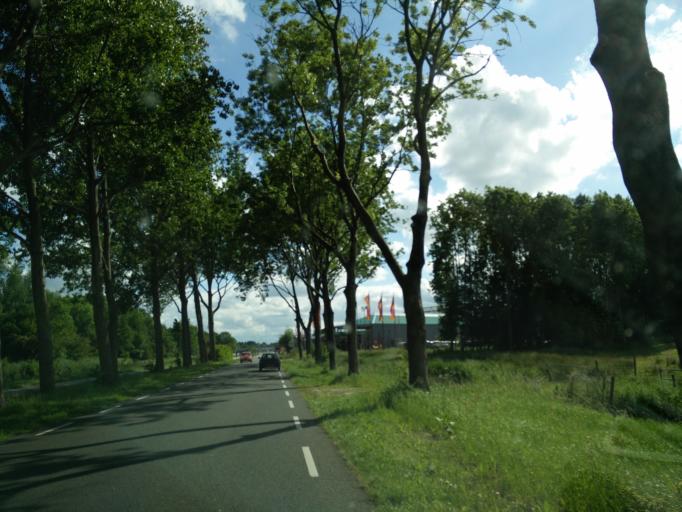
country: NL
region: Groningen
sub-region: Gemeente Groningen
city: Korrewegwijk
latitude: 53.2523
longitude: 6.5829
